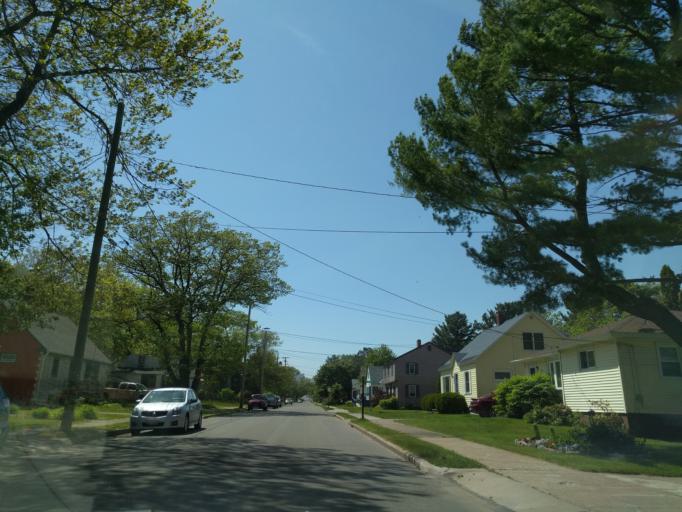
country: US
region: Michigan
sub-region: Marquette County
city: Marquette
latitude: 46.5547
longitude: -87.3871
